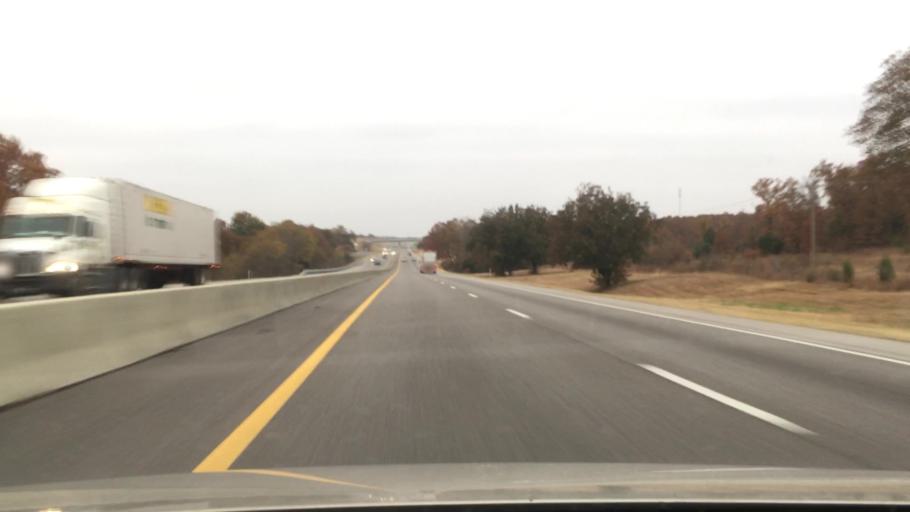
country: US
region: Oklahoma
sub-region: Lincoln County
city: Chandler
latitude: 35.7214
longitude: -96.8728
